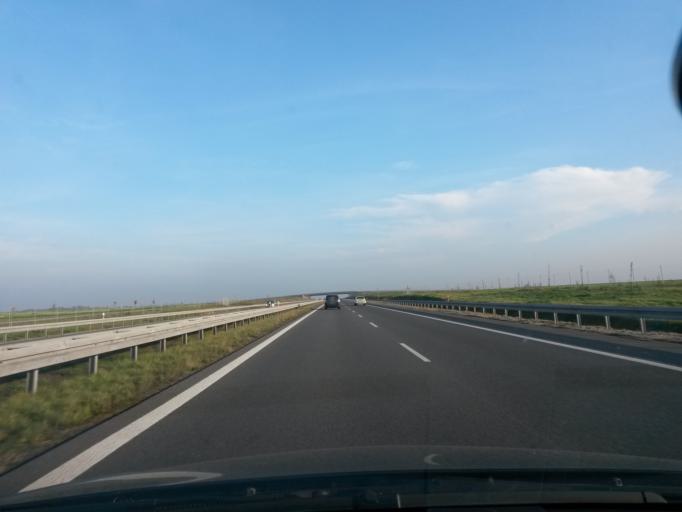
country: PL
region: Lower Silesian Voivodeship
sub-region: Powiat wroclawski
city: Dlugoleka
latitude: 51.2279
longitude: 17.2627
